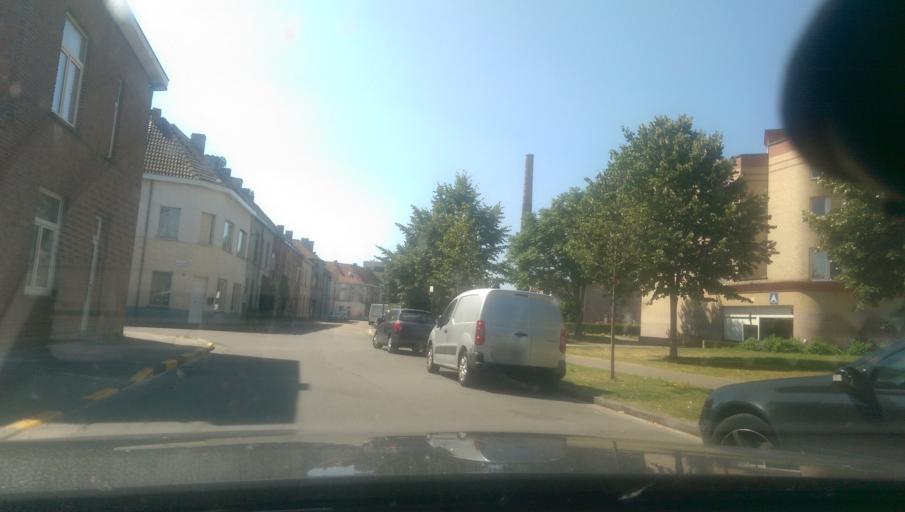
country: BE
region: Flanders
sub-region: Provincie Oost-Vlaanderen
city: Gent
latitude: 51.0624
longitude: 3.7162
